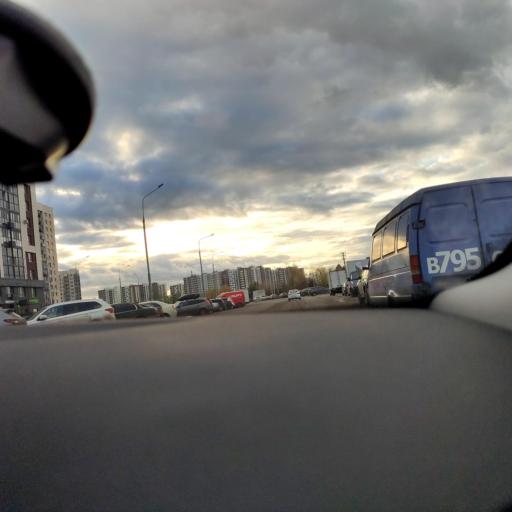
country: RU
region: Moskovskaya
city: Mosrentgen
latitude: 55.5947
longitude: 37.4582
